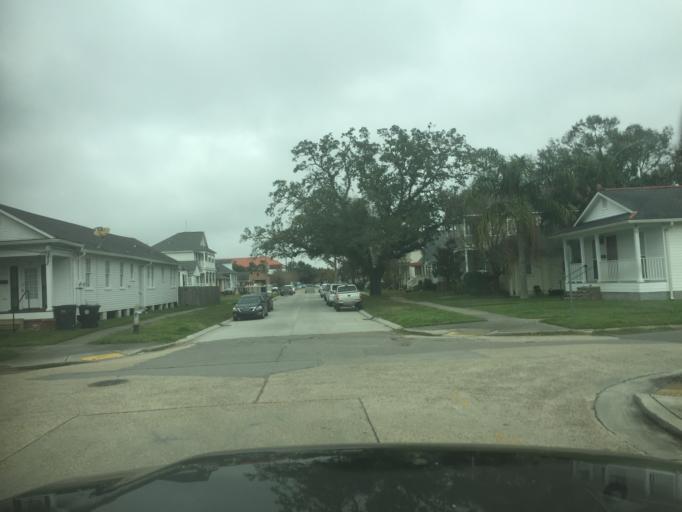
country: US
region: Louisiana
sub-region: Jefferson Parish
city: Metairie
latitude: 30.0025
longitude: -90.1060
